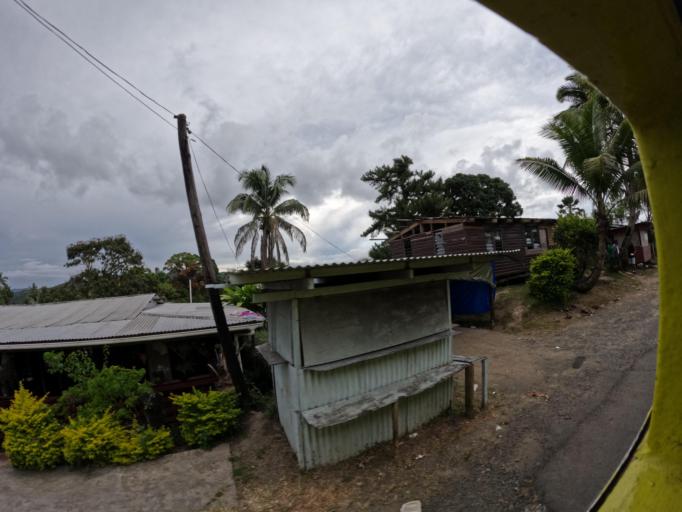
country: FJ
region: Central
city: Suva
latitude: -18.0811
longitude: 178.4565
